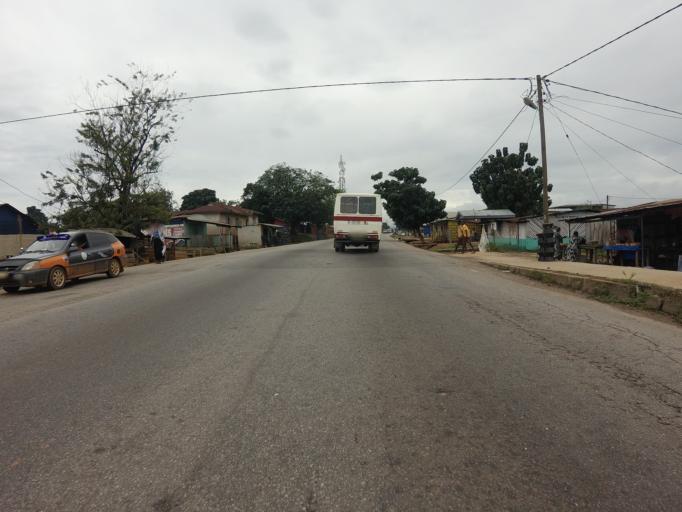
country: GH
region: Eastern
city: Begoro
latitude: 6.4346
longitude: -0.5851
